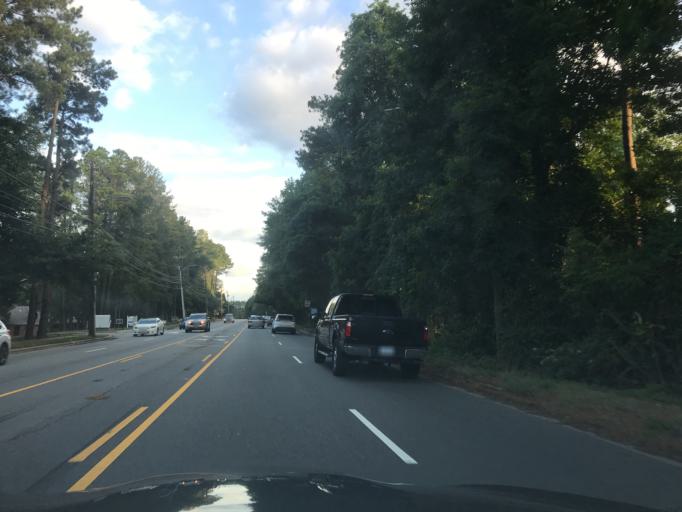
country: US
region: North Carolina
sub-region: Wake County
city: West Raleigh
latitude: 35.8279
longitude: -78.6345
